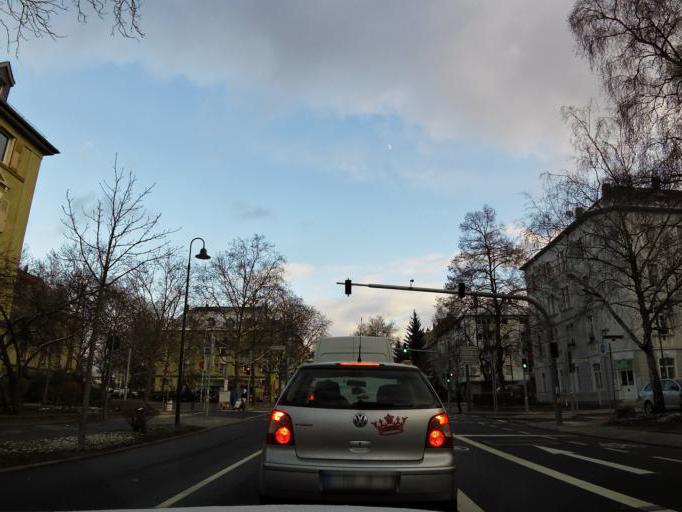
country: DE
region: Hesse
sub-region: Regierungsbezirk Darmstadt
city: Darmstadt
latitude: 49.8831
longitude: 8.6595
